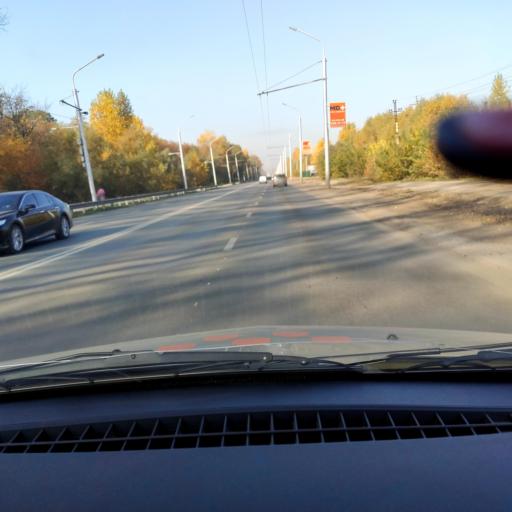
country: RU
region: Bashkortostan
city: Ufa
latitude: 54.7891
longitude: 56.1101
